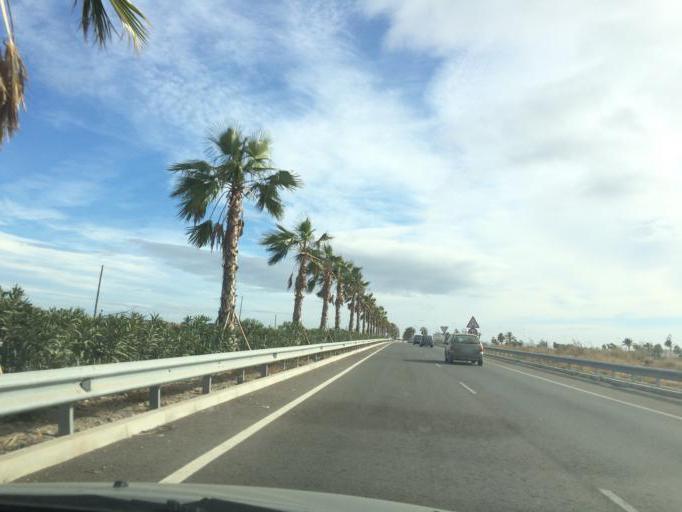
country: ES
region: Andalusia
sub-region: Provincia de Almeria
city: Retamar
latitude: 36.8521
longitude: -2.3242
